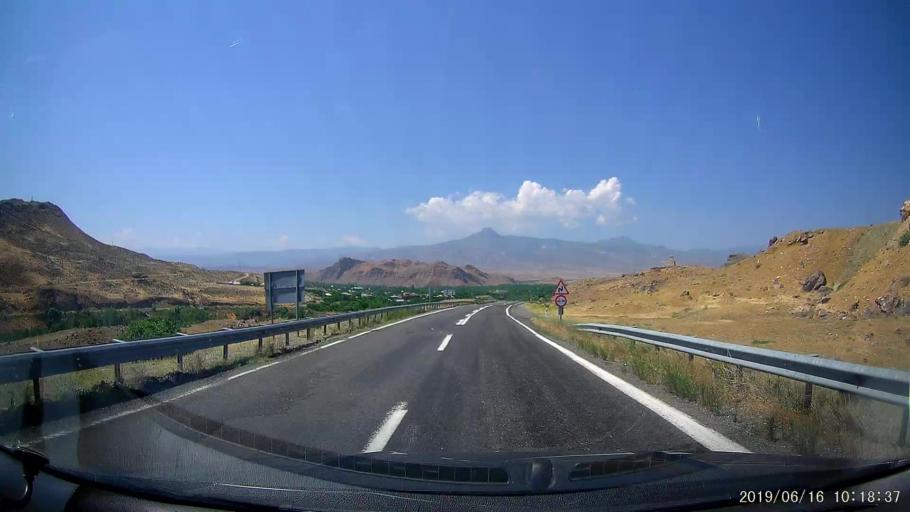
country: TR
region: Igdir
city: Tuzluca
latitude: 40.1586
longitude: 43.6659
